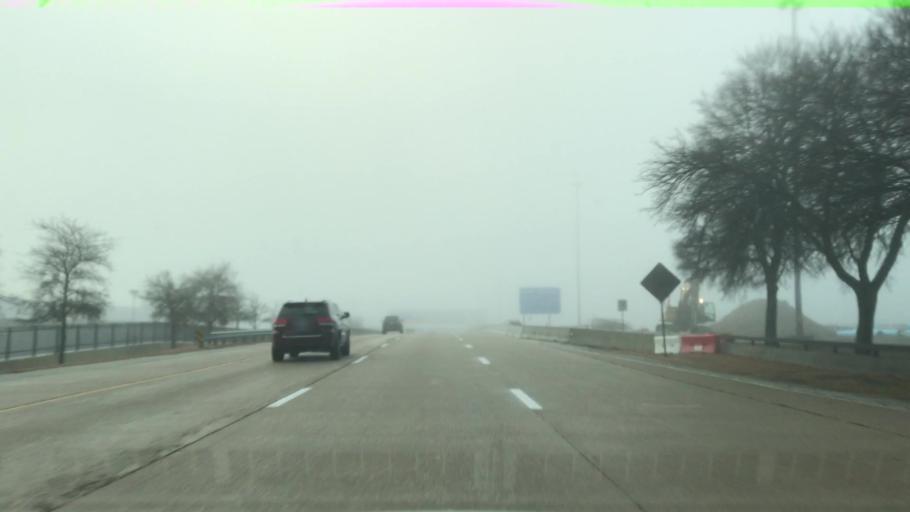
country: US
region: Texas
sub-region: Tarrant County
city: Grapevine
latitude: 32.9130
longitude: -97.0410
